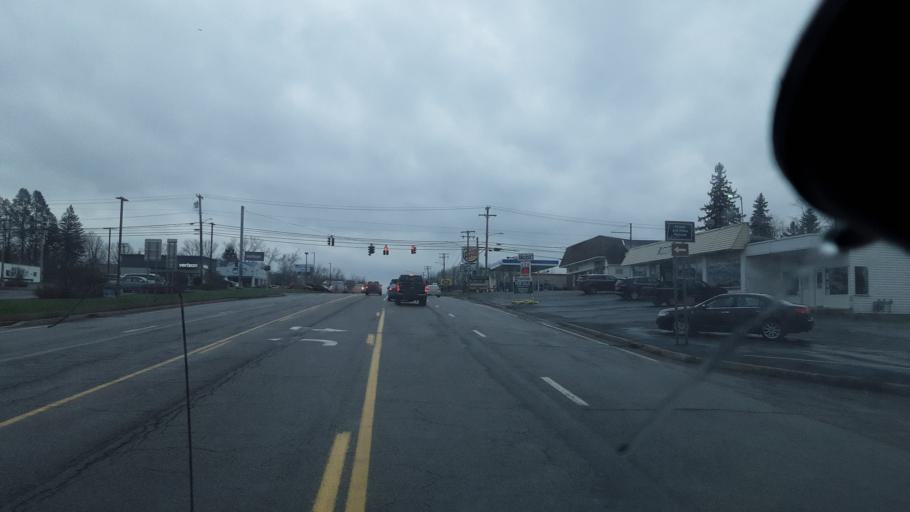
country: US
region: New York
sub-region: Cattaraugus County
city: Yorkshire
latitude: 42.5313
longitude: -78.4786
